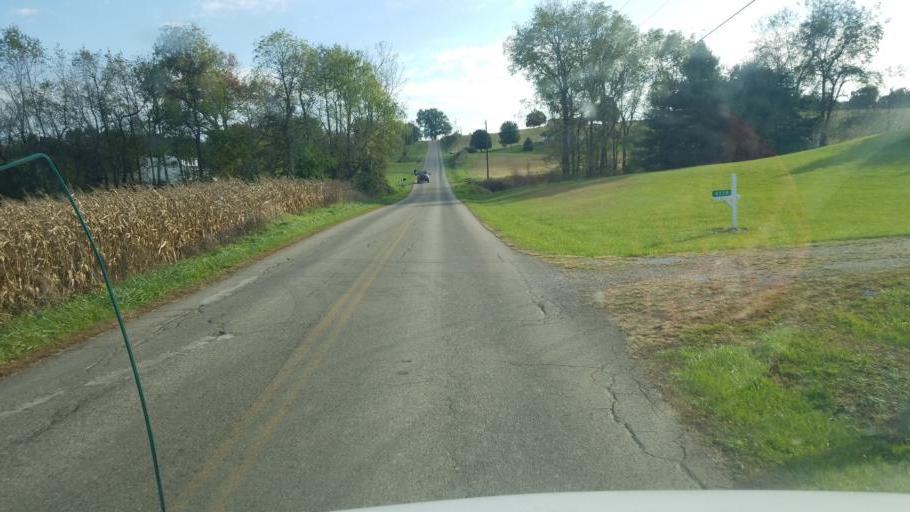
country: US
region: Ohio
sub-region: Wayne County
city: Shreve
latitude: 40.6577
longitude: -82.0770
